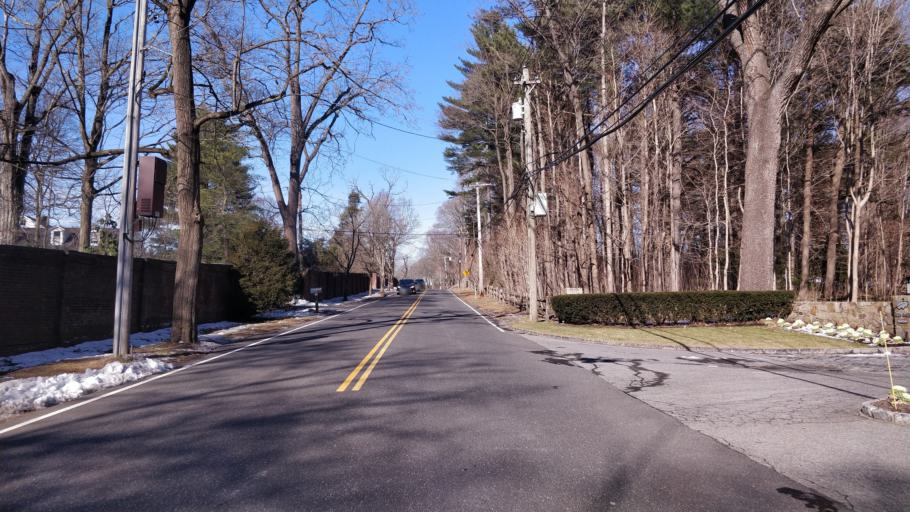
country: US
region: New York
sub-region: Nassau County
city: Old Westbury
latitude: 40.7895
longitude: -73.5884
